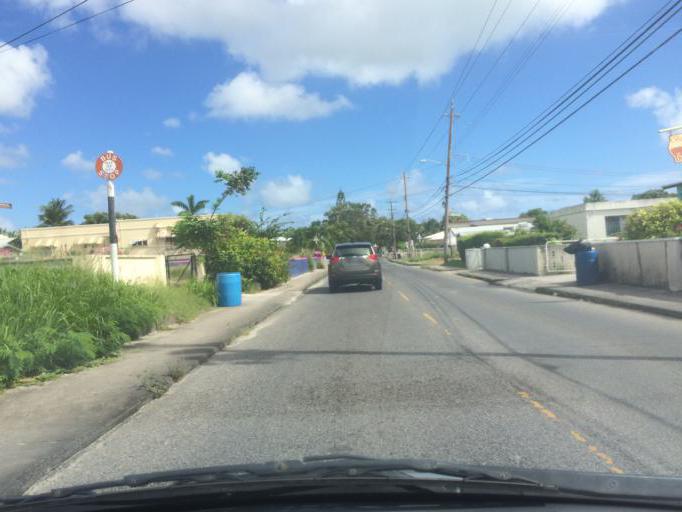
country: BB
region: Christ Church
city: Oistins
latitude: 13.0682
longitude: -59.5573
